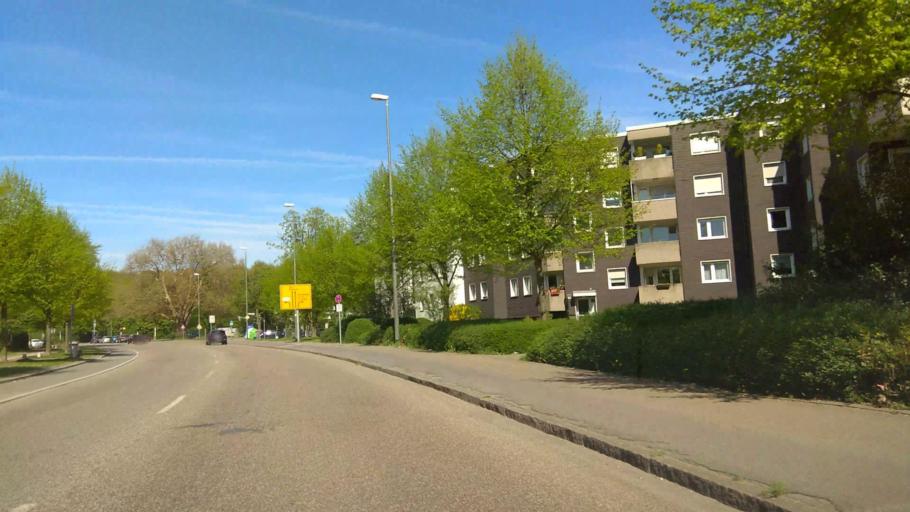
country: DE
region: North Rhine-Westphalia
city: Herten
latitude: 51.5784
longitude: 7.0670
